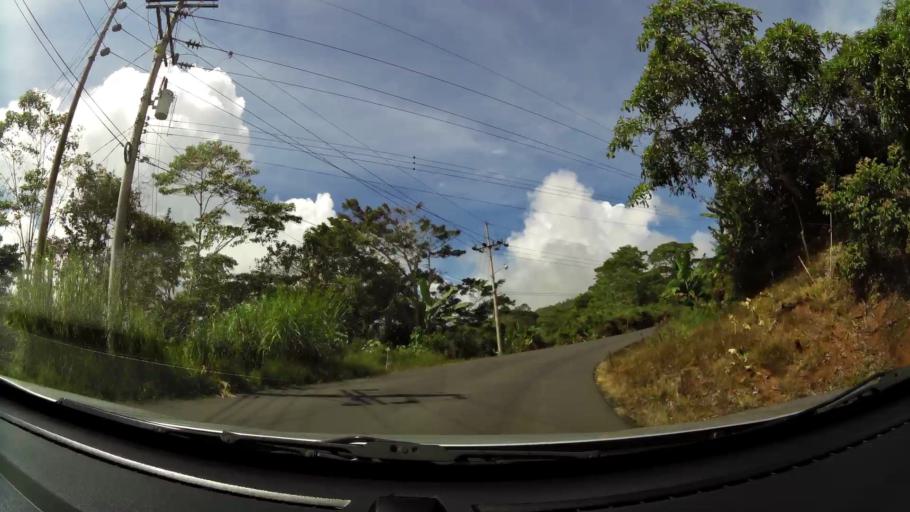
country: CR
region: San Jose
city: San Isidro
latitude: 9.3255
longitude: -83.7458
